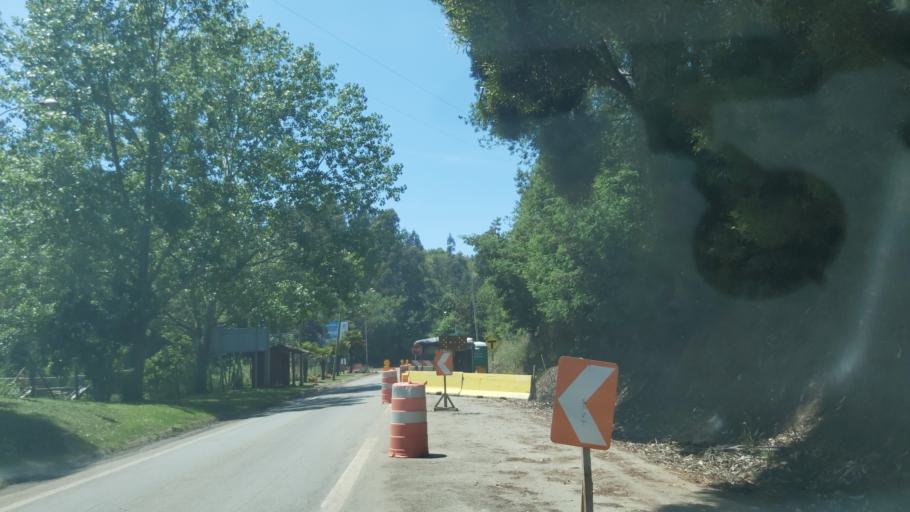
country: CL
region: Maule
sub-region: Provincia de Cauquenes
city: Cauquenes
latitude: -35.7940
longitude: -72.5418
